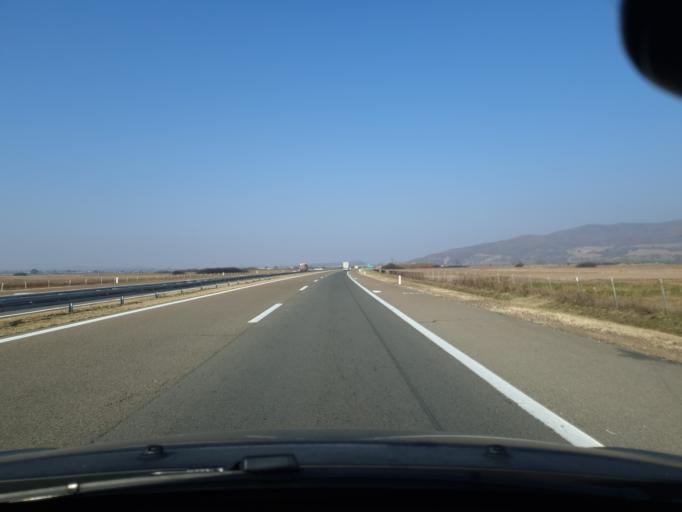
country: RS
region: Central Serbia
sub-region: Nisavski Okrug
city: Doljevac
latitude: 43.1774
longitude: 21.8657
